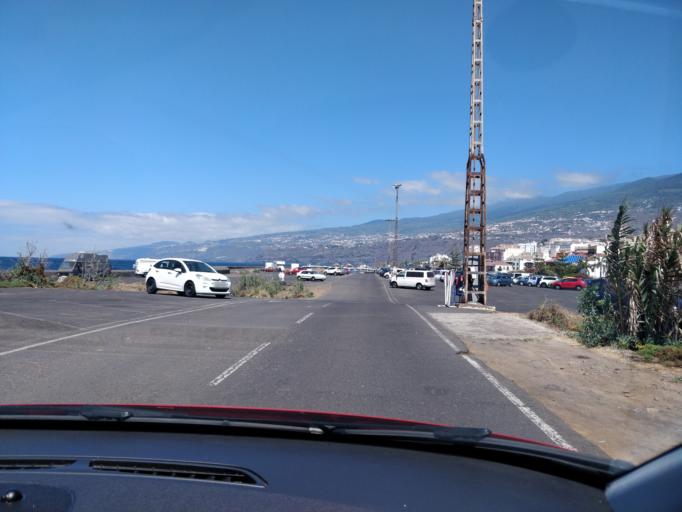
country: ES
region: Canary Islands
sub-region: Provincia de Santa Cruz de Tenerife
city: Puerto de la Cruz
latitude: 28.4182
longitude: -16.5542
